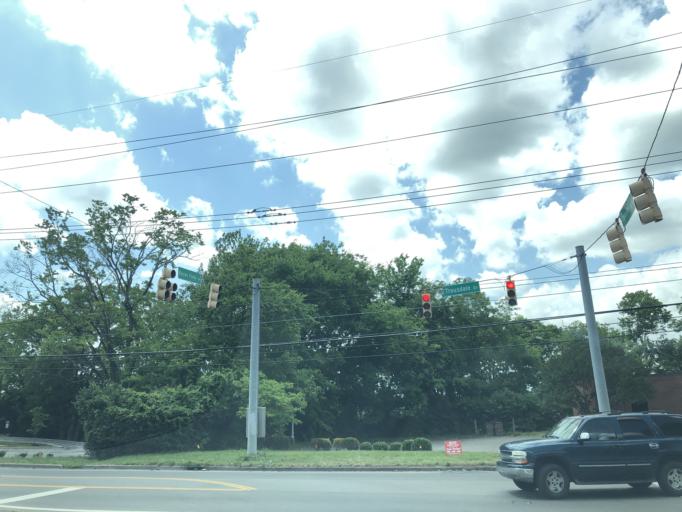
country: US
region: Tennessee
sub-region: Davidson County
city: Oak Hill
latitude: 36.0850
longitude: -86.7552
